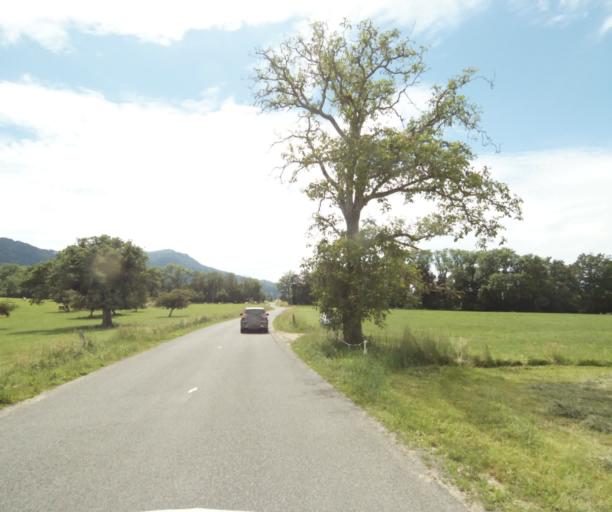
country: FR
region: Rhone-Alpes
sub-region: Departement de la Haute-Savoie
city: Bons-en-Chablais
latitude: 46.2728
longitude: 6.4062
